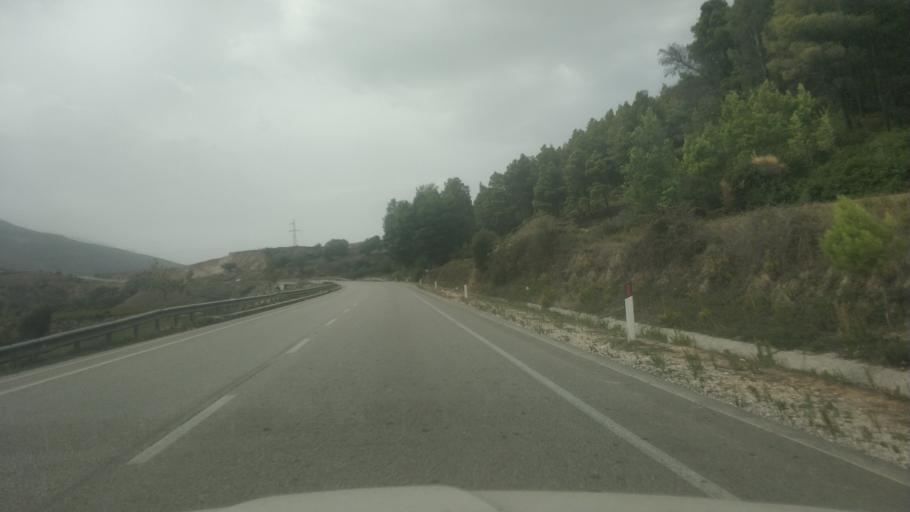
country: AL
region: Gjirokaster
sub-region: Rrethi i Tepelenes
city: Memaliaj
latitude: 40.3552
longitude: 19.9477
